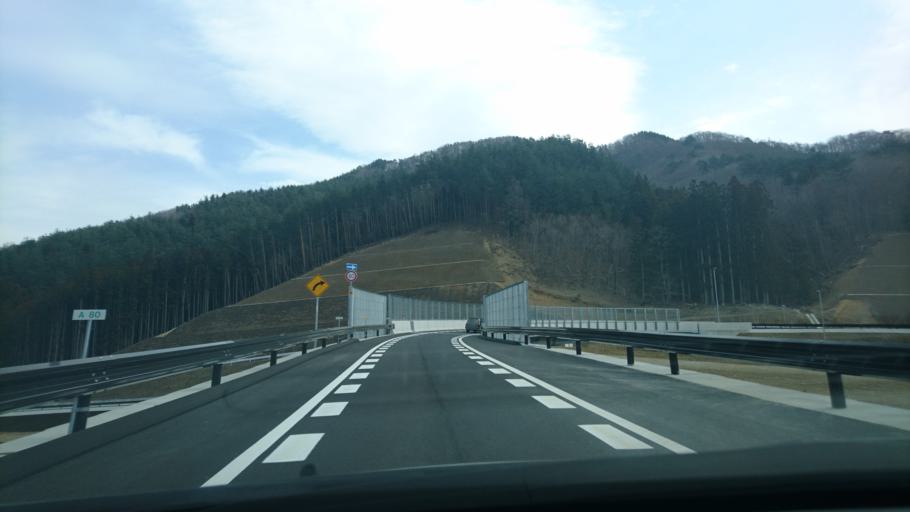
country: JP
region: Iwate
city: Kamaishi
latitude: 39.2546
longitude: 141.8362
